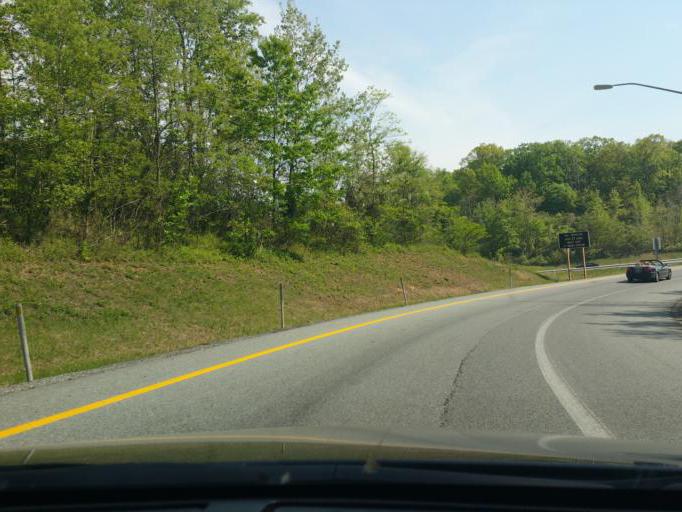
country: US
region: Maryland
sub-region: Cecil County
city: Perryville
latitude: 39.5953
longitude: -76.0651
